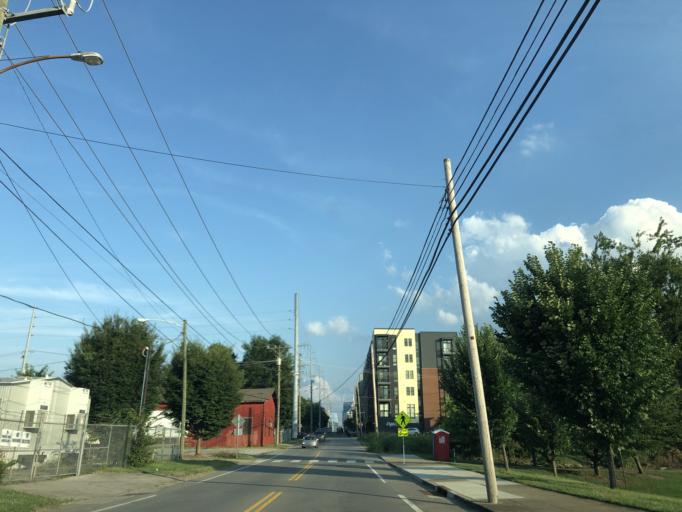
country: US
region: Tennessee
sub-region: Davidson County
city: Nashville
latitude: 36.1816
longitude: -86.7890
